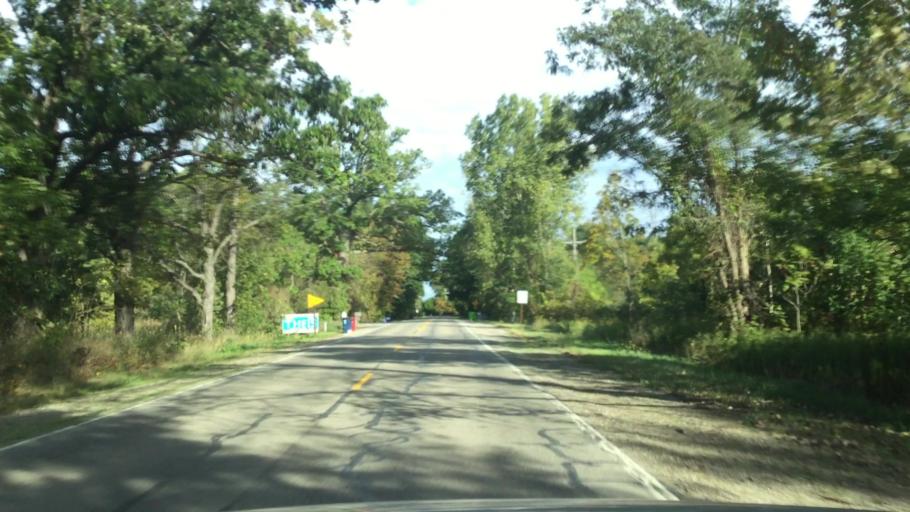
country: US
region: Michigan
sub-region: Livingston County
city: Howell
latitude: 42.5600
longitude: -83.8888
